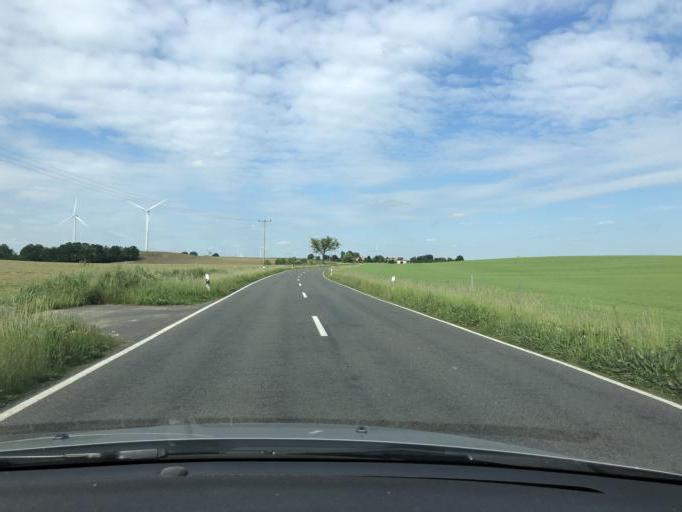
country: DE
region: Saxony
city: Nerchau
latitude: 51.2293
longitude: 12.8114
